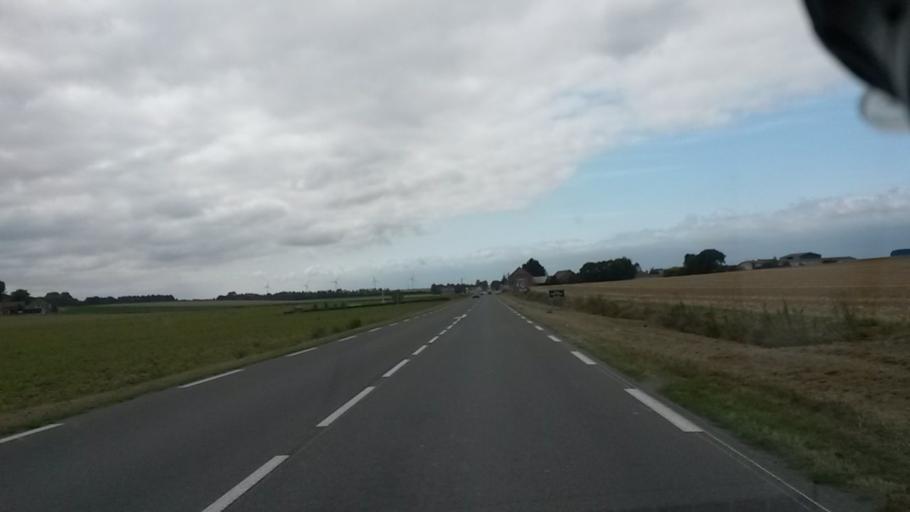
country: FR
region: Nord-Pas-de-Calais
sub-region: Departement du Pas-de-Calais
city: Bourlon
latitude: 50.1605
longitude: 3.1301
